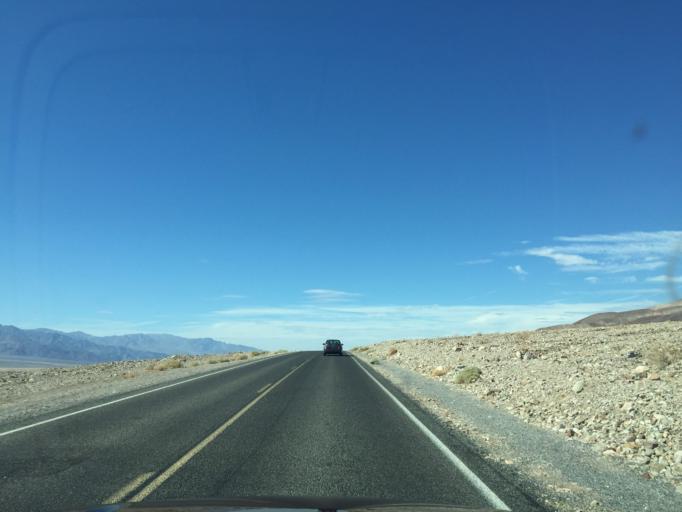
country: US
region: Nevada
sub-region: Nye County
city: Beatty
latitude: 36.2569
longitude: -116.7767
